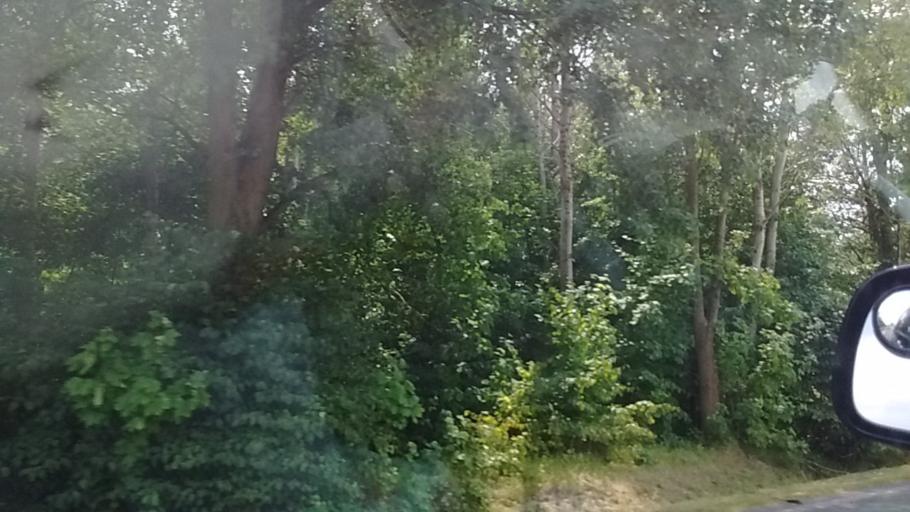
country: PL
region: Subcarpathian Voivodeship
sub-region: Powiat lezajski
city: Brzoza Krolewska
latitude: 50.2011
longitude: 22.3579
